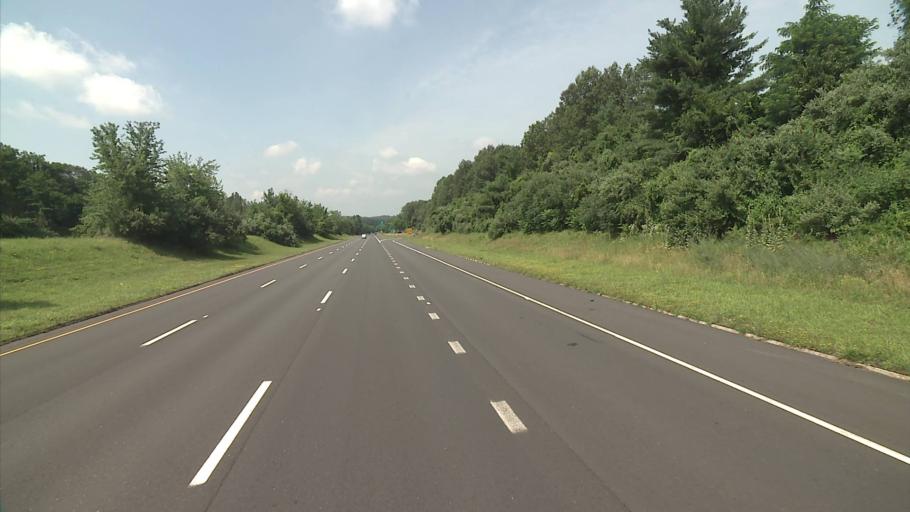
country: US
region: Connecticut
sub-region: Hartford County
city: Manchester
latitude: 41.7647
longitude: -72.4923
